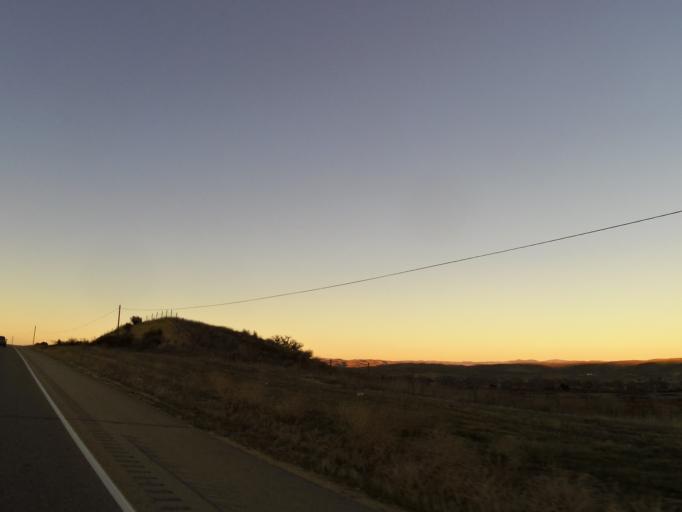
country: US
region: California
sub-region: San Luis Obispo County
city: Lake Nacimiento
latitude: 35.9820
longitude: -120.9022
